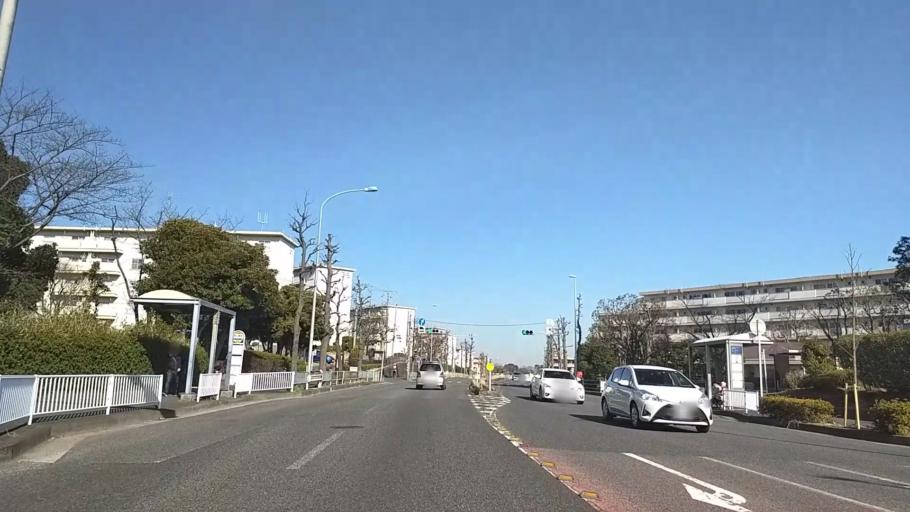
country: JP
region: Kanagawa
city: Yokohama
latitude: 35.3814
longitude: 139.5935
